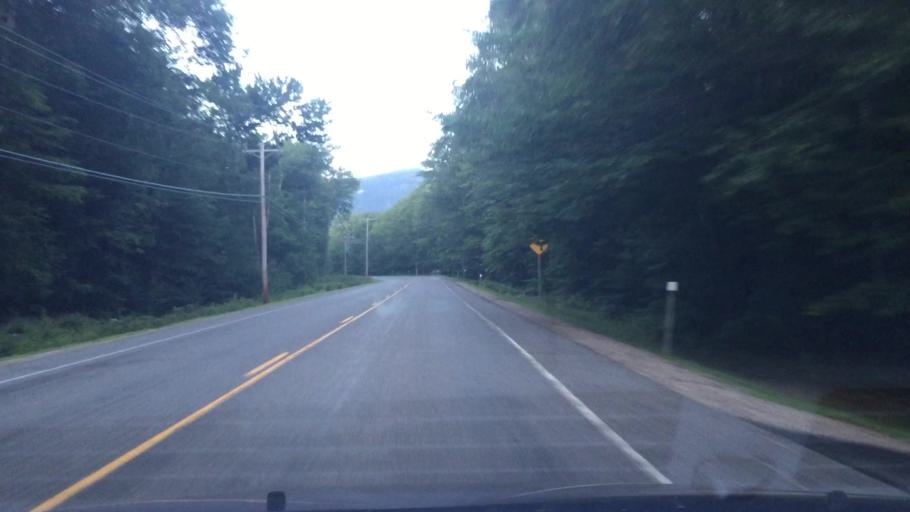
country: US
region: New Hampshire
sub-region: Grafton County
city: Woodstock
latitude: 44.0622
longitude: -71.6154
